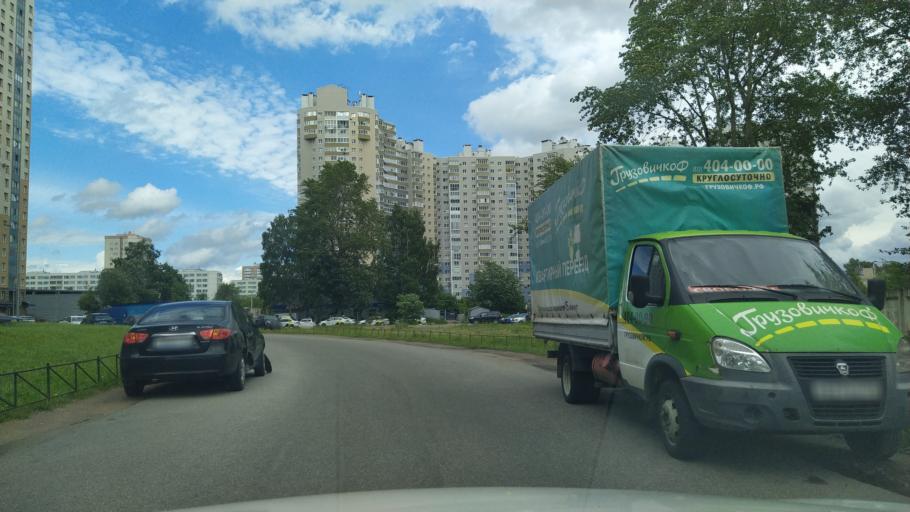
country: RU
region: Leningrad
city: Akademicheskoe
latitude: 60.0119
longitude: 30.3894
